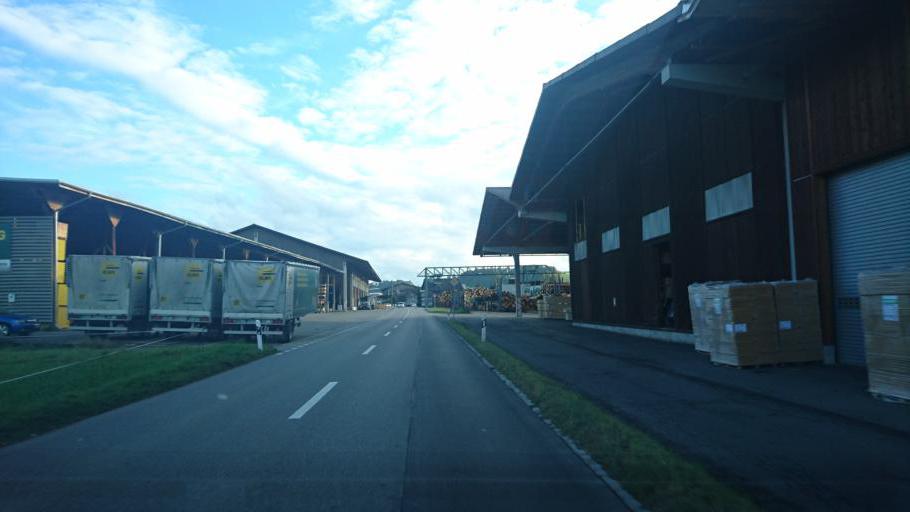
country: CH
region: Bern
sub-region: Bern-Mittelland District
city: Vechigen
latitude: 46.9419
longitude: 7.5575
